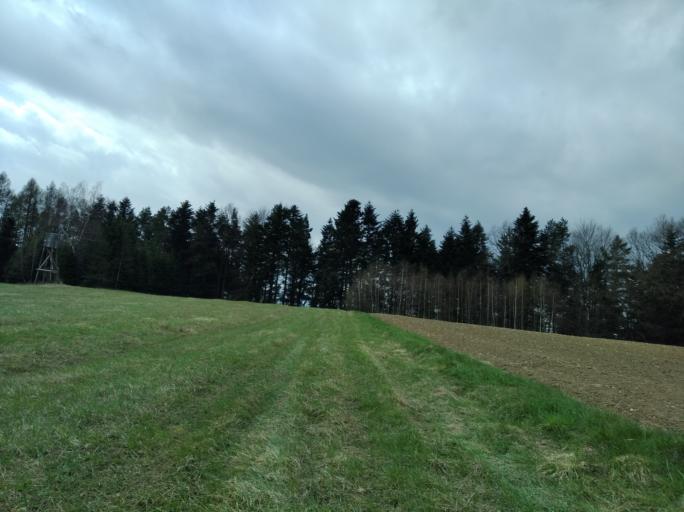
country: PL
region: Subcarpathian Voivodeship
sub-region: Powiat strzyzowski
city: Wysoka Strzyzowska
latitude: 49.8040
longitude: 21.7689
